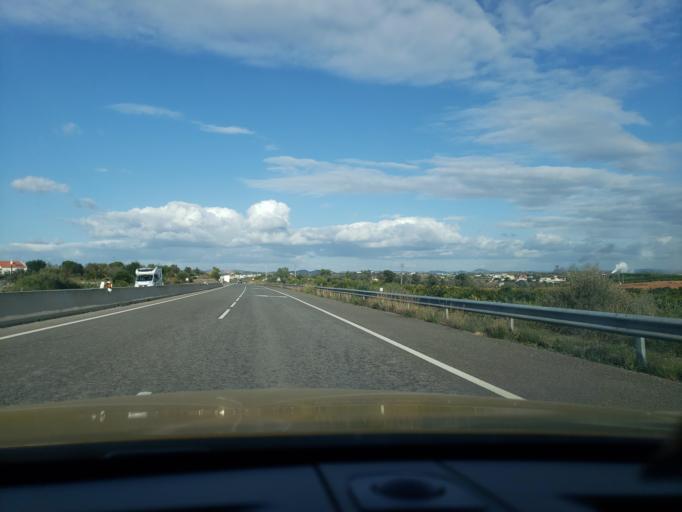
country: PT
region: Faro
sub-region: Silves
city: Silves
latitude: 37.1625
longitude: -8.4451
